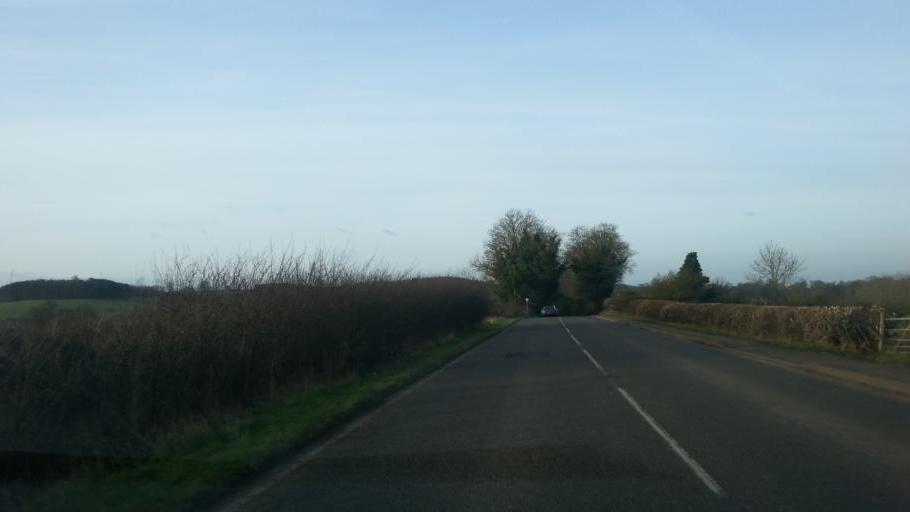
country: GB
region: England
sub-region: Lincolnshire
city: Barrowby
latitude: 52.8835
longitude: -0.6988
